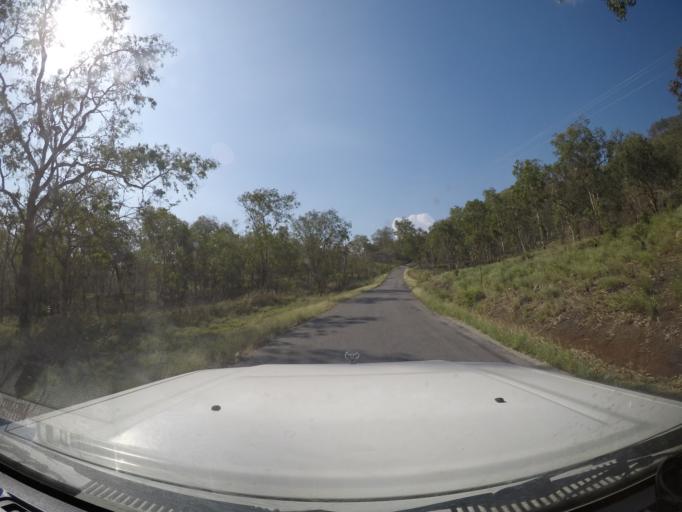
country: PG
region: Central Province
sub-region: Rigo
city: Kwikila
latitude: -9.8711
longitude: 147.5651
